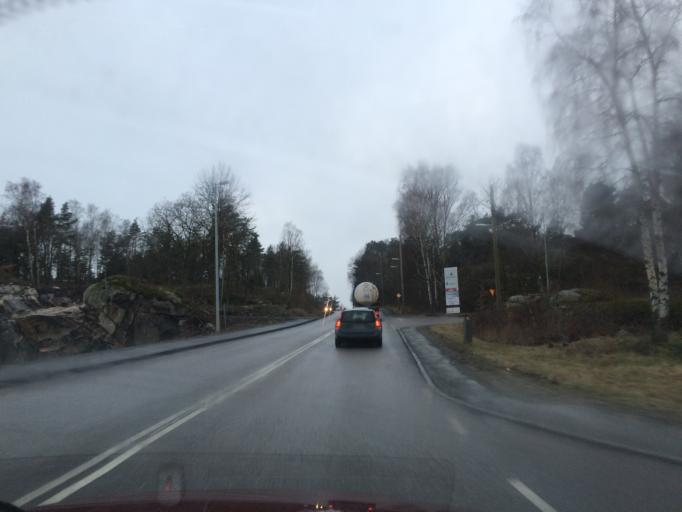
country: SE
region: Vaestra Goetaland
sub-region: Goteborg
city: Majorna
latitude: 57.7055
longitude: 11.8487
